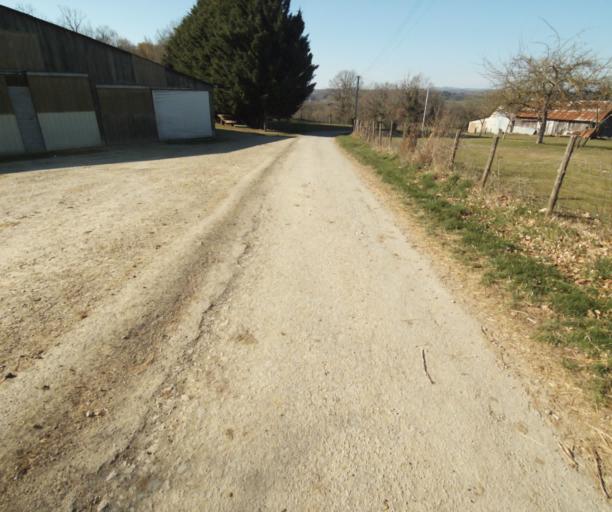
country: FR
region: Limousin
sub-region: Departement de la Correze
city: Chamboulive
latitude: 45.4722
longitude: 1.6855
